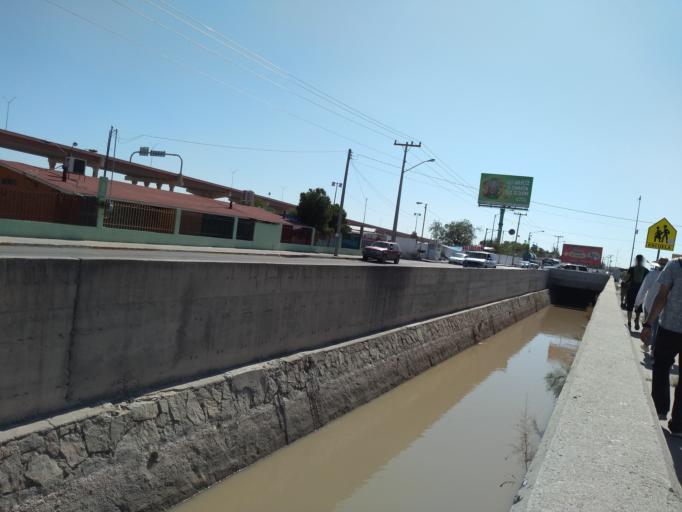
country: US
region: Texas
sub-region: El Paso County
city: El Paso
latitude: 31.7556
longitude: -106.5011
